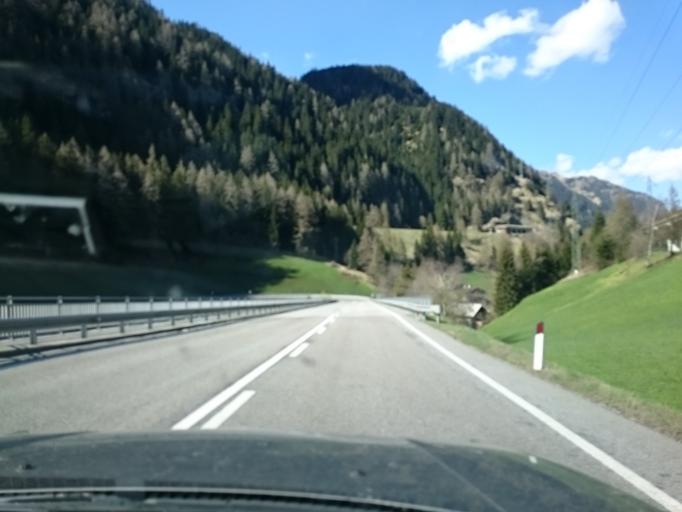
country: IT
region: Trentino-Alto Adige
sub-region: Bolzano
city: Colle Isarco
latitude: 46.9547
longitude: 11.4571
